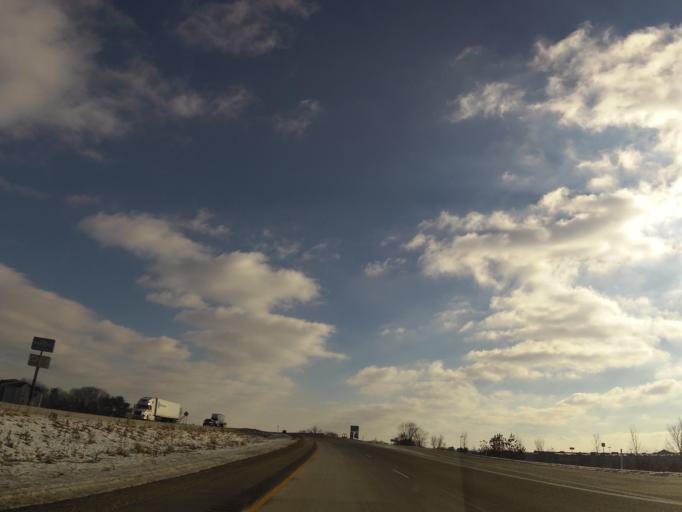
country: US
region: Wisconsin
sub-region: Monroe County
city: Tomah
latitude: 44.0234
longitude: -90.5091
